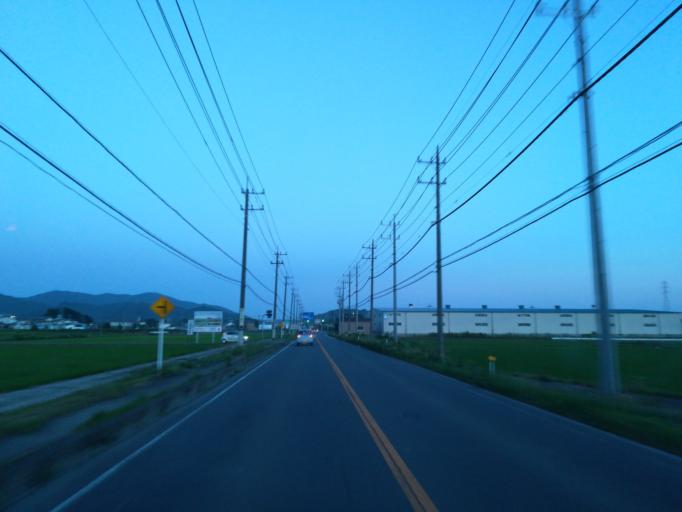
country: JP
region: Ibaraki
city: Tsukuba
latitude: 36.2099
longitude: 140.0720
